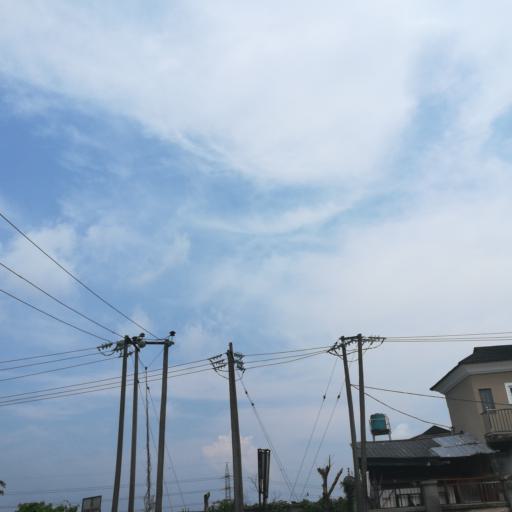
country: NG
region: Rivers
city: Port Harcourt
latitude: 4.8576
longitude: 7.0223
